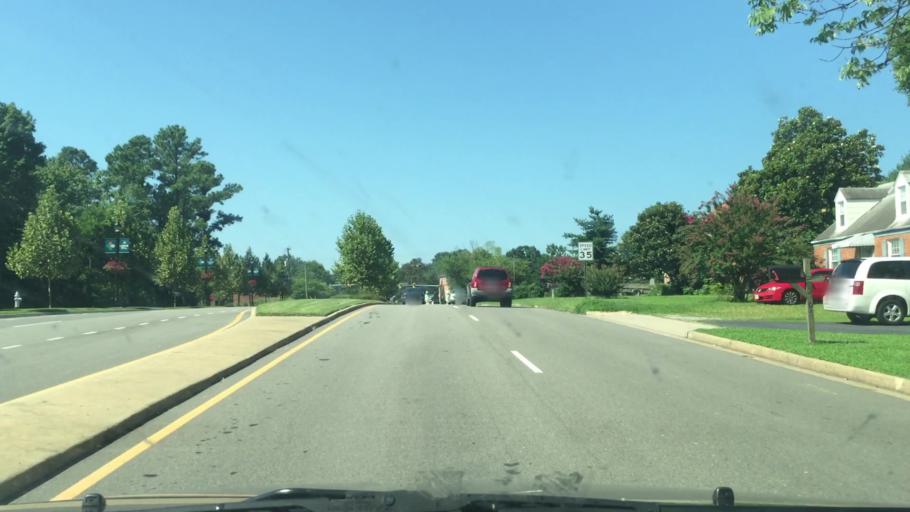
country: US
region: Virginia
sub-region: Henrico County
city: Dumbarton
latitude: 37.5915
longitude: -77.5022
